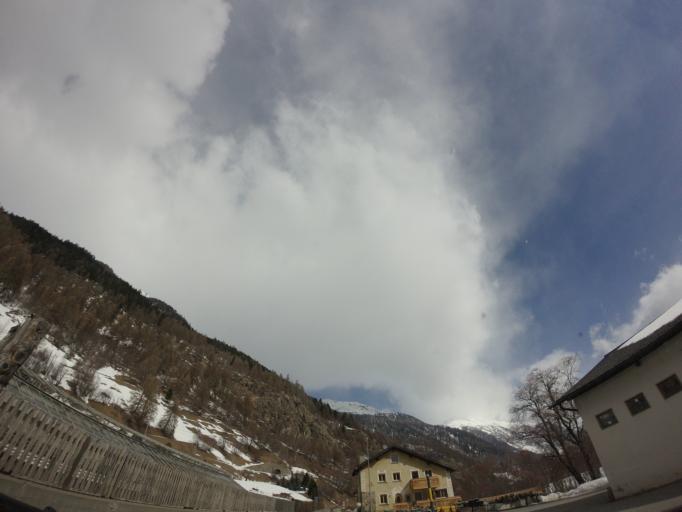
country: CH
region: Grisons
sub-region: Inn District
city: Zernez
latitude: 46.7525
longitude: 10.0812
